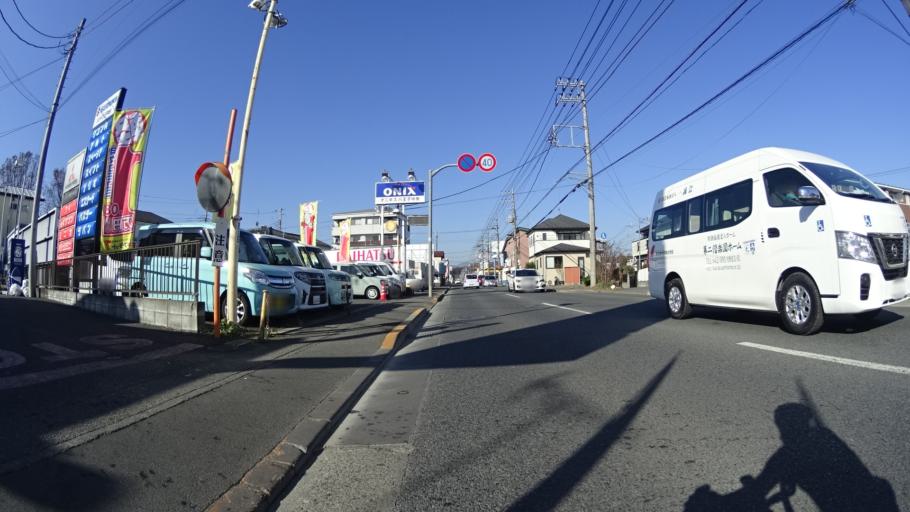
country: JP
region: Tokyo
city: Hachioji
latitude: 35.6778
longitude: 139.2853
